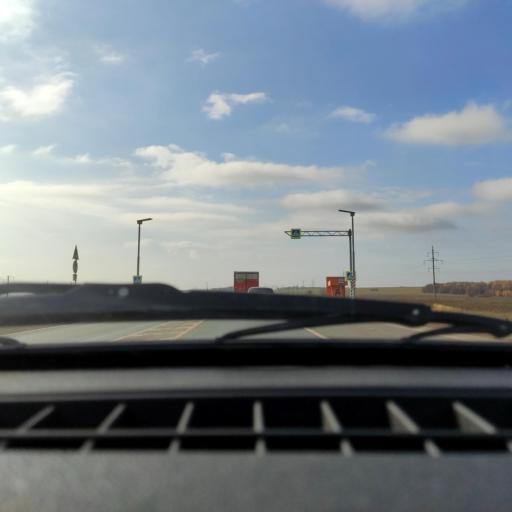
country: RU
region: Bashkortostan
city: Kabakovo
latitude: 54.6992
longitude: 56.2134
